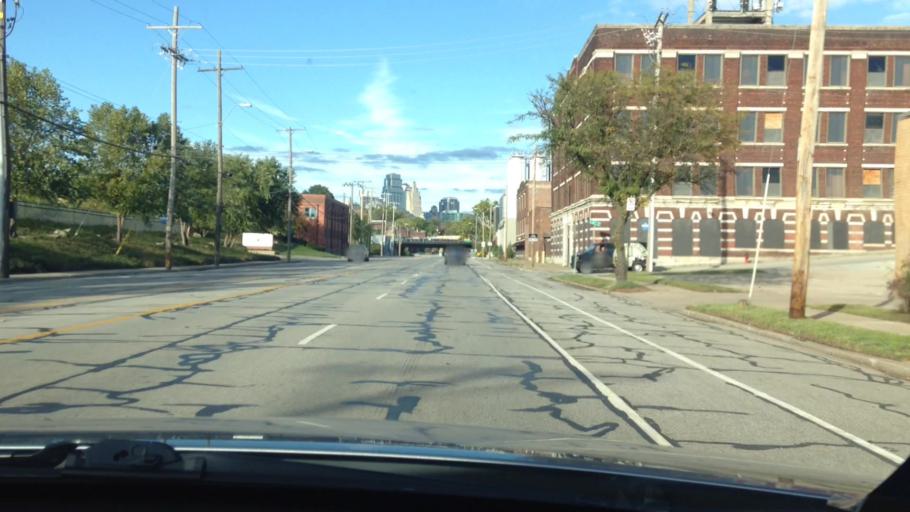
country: US
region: Missouri
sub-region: Jackson County
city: Kansas City
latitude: 39.0805
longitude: -94.5985
